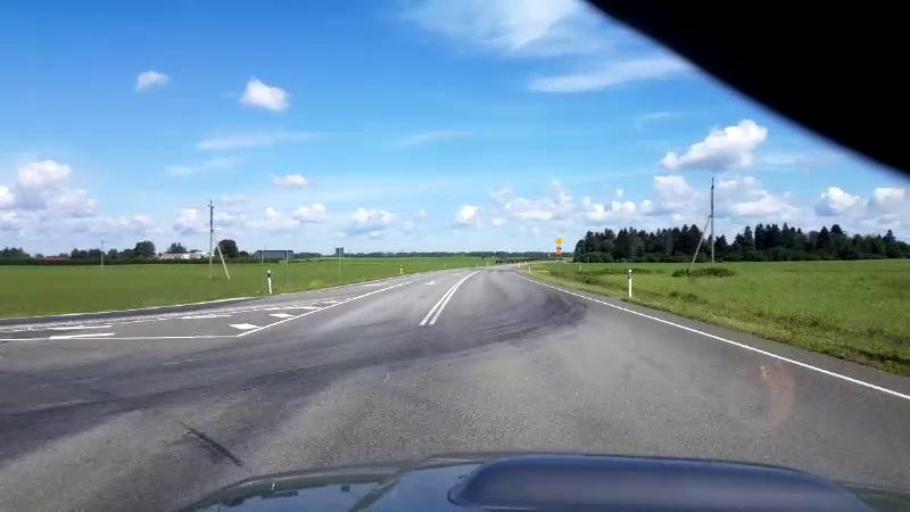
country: EE
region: Jaervamaa
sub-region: Jaerva-Jaani vald
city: Jarva-Jaani
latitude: 59.1710
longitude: 25.7576
